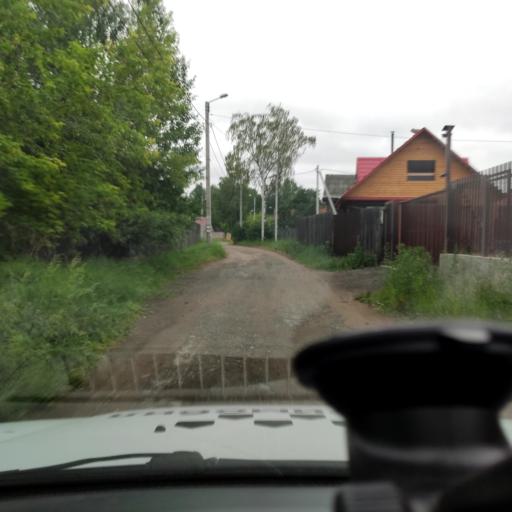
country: RU
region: Perm
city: Perm
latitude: 58.0309
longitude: 56.2246
